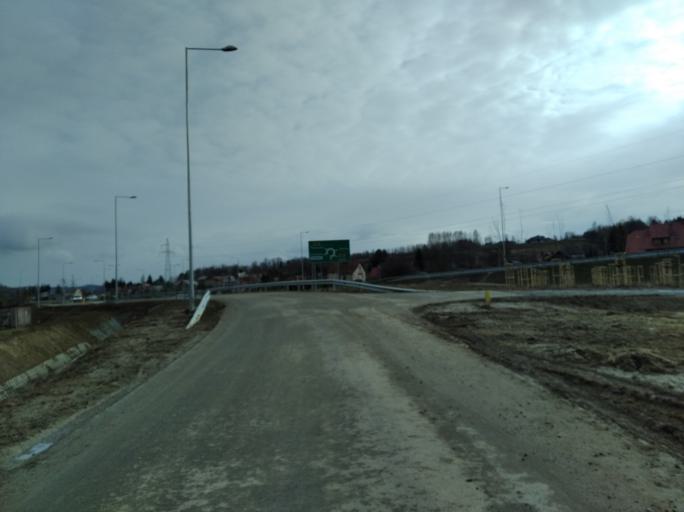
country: PL
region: Subcarpathian Voivodeship
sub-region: Powiat strzyzowski
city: Strzyzow
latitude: 49.8636
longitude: 21.7826
